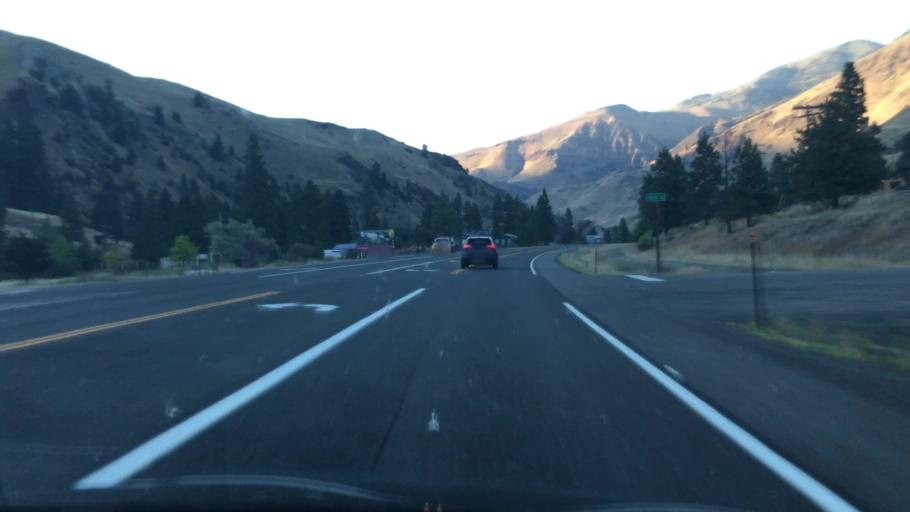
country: US
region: Idaho
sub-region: Valley County
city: McCall
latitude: 45.3077
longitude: -116.3616
